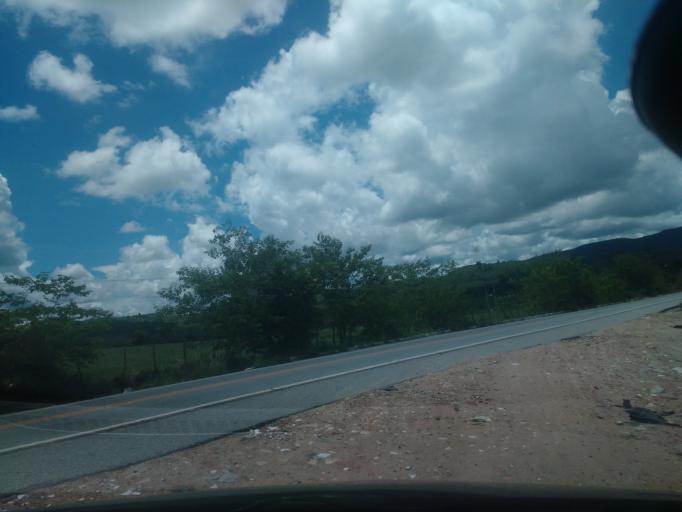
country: BR
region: Alagoas
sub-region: Uniao Dos Palmares
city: Uniao dos Palmares
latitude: -9.1338
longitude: -36.0257
